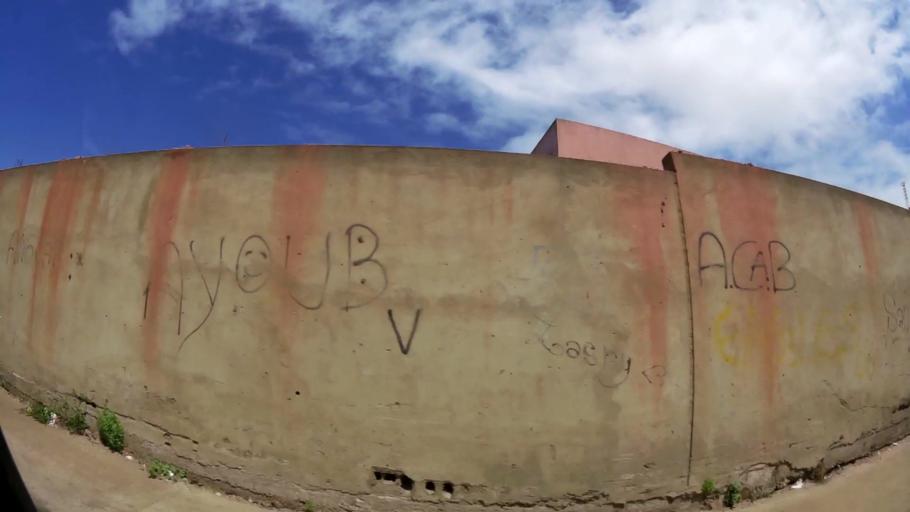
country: MA
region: Grand Casablanca
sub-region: Mediouna
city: Tit Mellil
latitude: 33.6042
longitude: -7.5266
